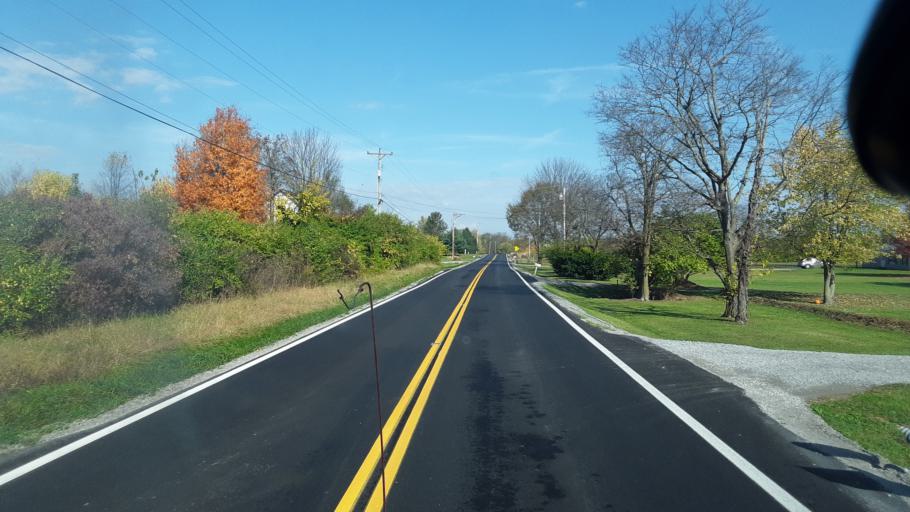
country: US
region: Ohio
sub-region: Highland County
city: Leesburg
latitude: 39.3594
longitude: -83.5890
